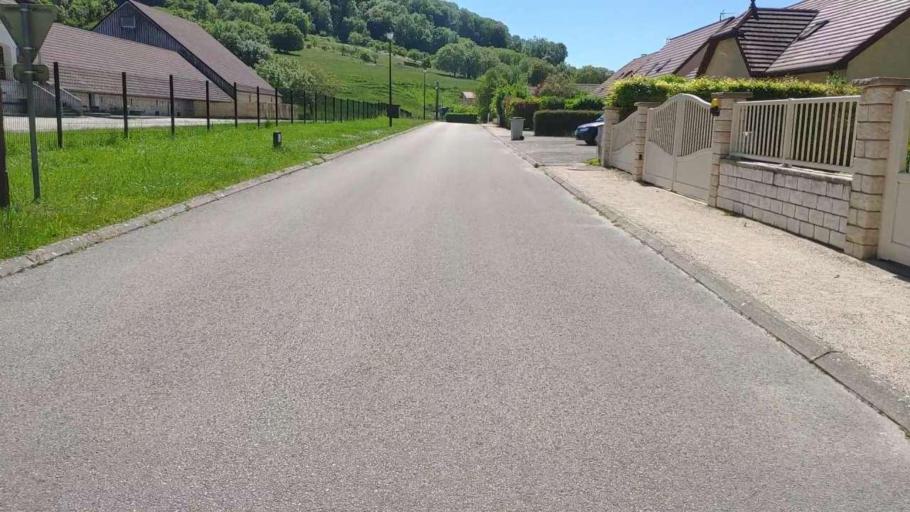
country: FR
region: Franche-Comte
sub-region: Departement du Jura
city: Perrigny
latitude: 46.7509
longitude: 5.6179
